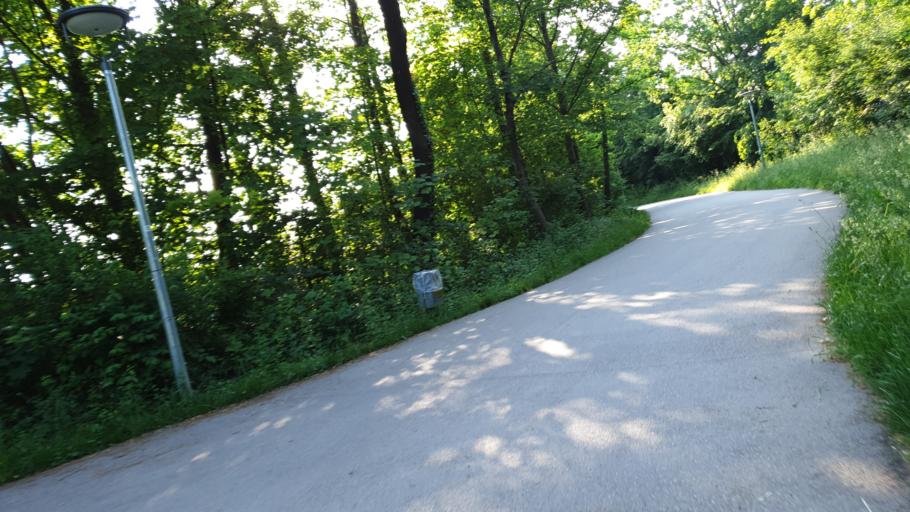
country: DE
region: Bavaria
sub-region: Upper Bavaria
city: Pasing
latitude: 48.1619
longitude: 11.4711
